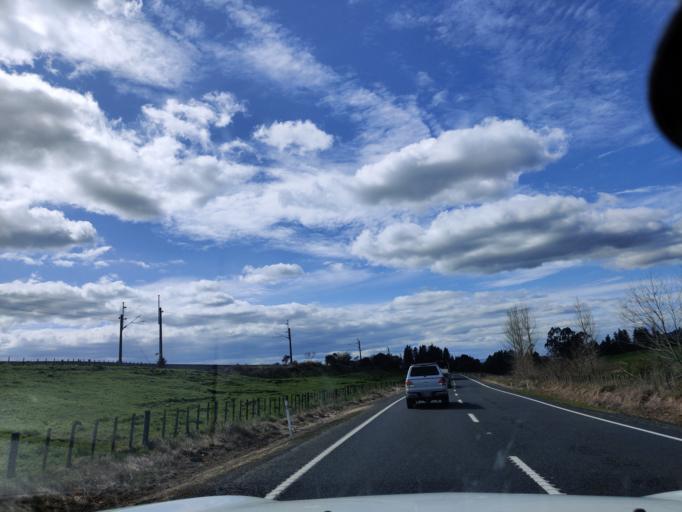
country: NZ
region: Waikato
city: Turangi
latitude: -39.0312
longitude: 175.3815
